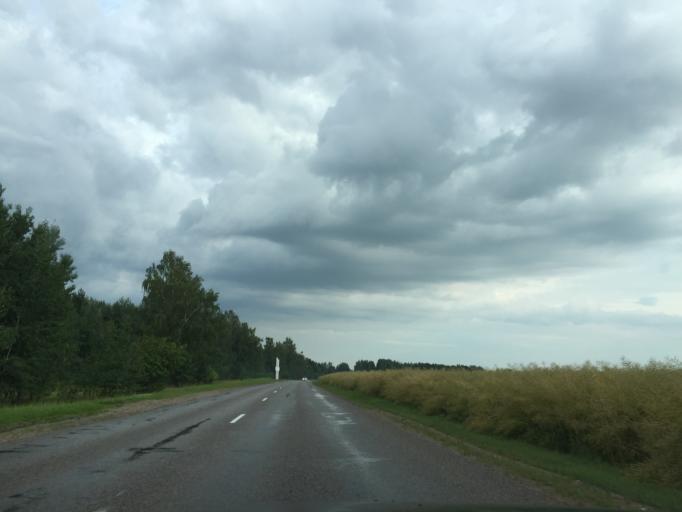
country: LV
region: Dobeles Rajons
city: Dobele
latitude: 56.6031
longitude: 23.2780
